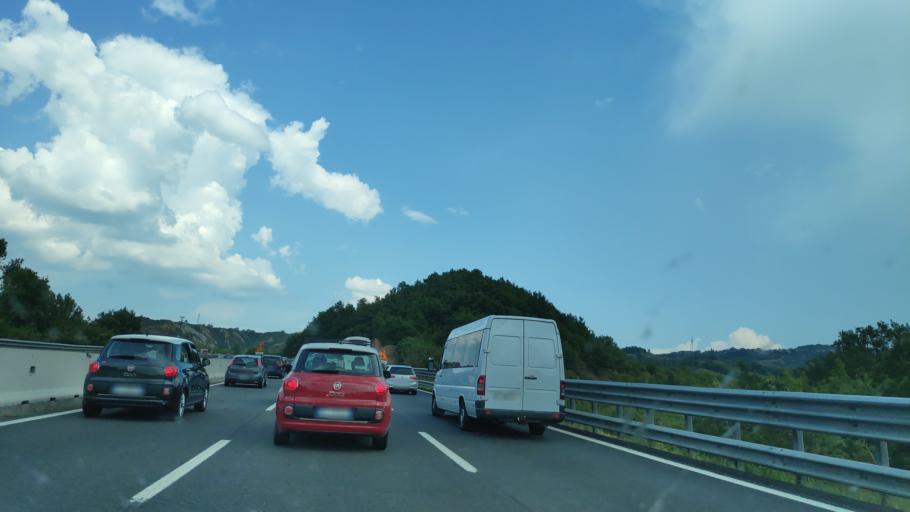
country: IT
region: Umbria
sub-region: Provincia di Terni
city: Ficulle
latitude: 42.8237
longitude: 12.0402
